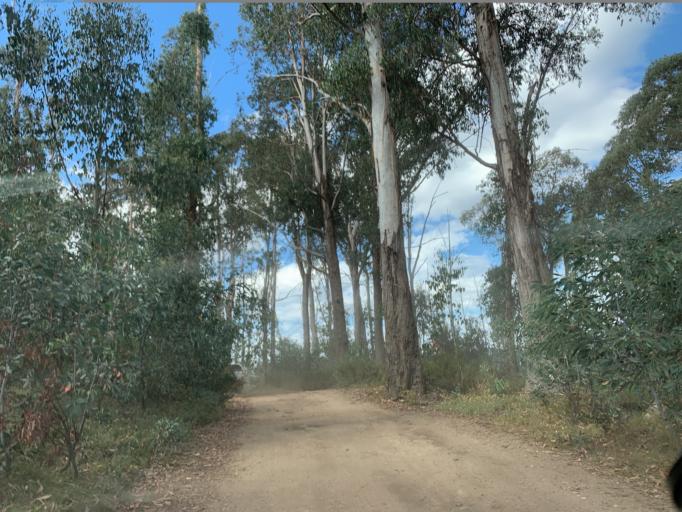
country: AU
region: Victoria
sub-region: Mansfield
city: Mansfield
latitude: -37.1013
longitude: 146.5444
